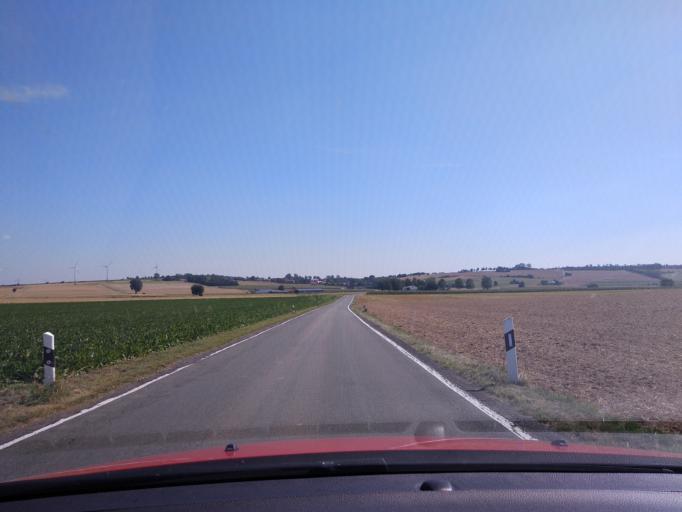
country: DE
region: North Rhine-Westphalia
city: Brakel
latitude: 51.6504
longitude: 9.1668
